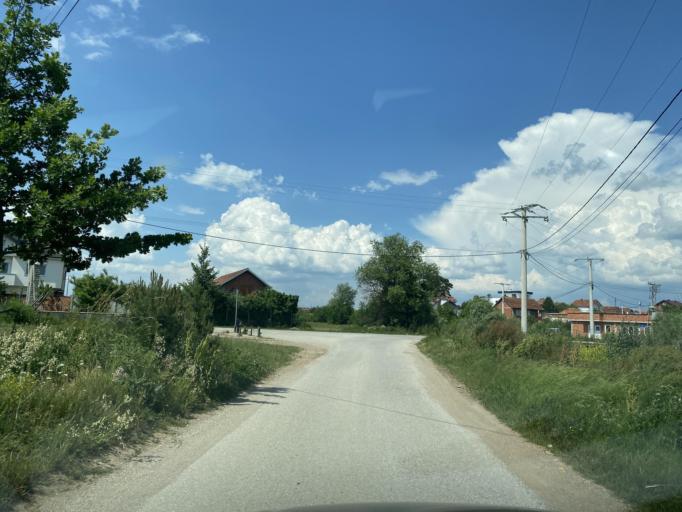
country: XK
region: Pristina
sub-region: Podujevo
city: Podujeva
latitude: 42.8679
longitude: 21.1766
